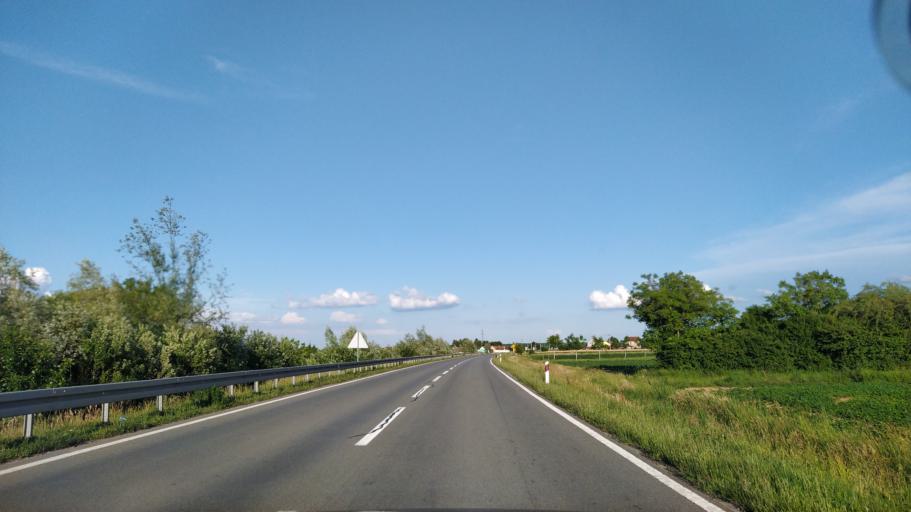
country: HR
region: Virovitick-Podravska
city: Slatina
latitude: 45.7166
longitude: 17.7059
